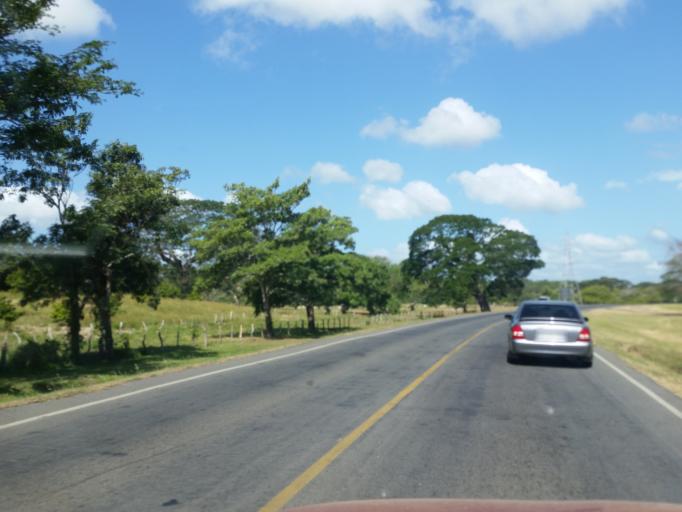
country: NI
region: Granada
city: Nandaime
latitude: 11.7169
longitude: -86.0123
